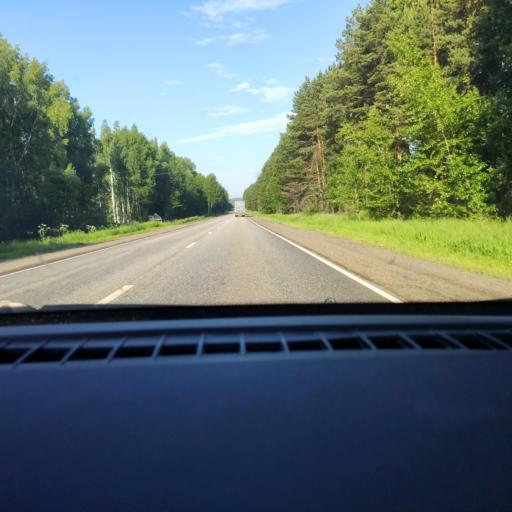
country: RU
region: Udmurtiya
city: Khokhryaki
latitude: 56.9455
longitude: 53.6050
